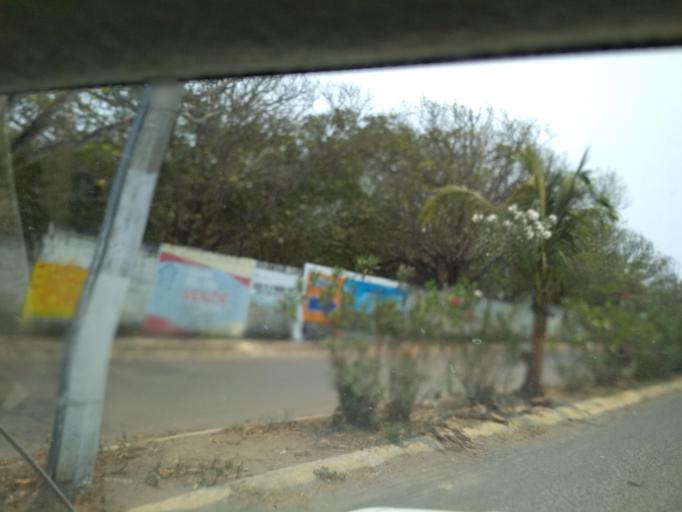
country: MX
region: Veracruz
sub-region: Veracruz
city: Las Amapolas
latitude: 19.1548
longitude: -96.2099
